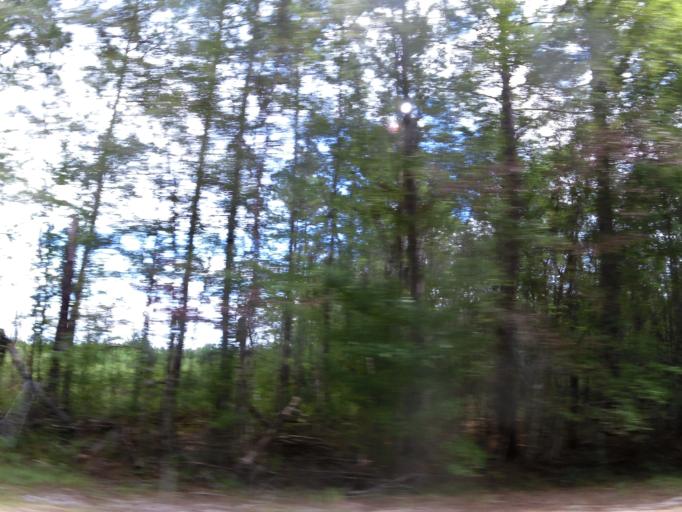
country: US
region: Georgia
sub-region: Brantley County
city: Nahunta
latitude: 31.0680
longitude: -82.0131
